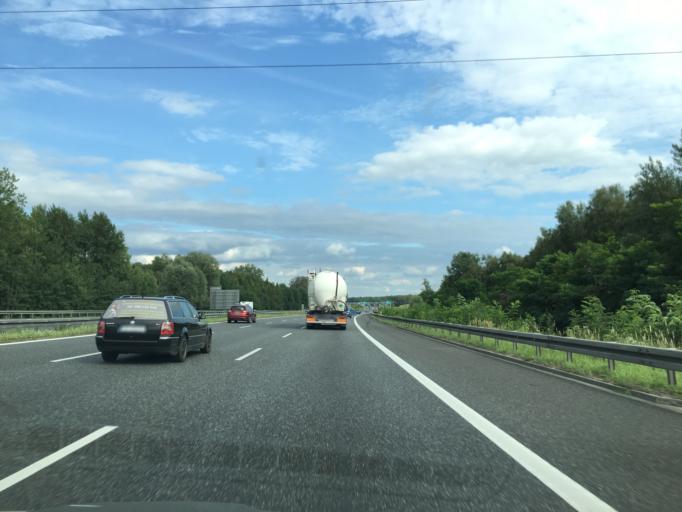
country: PL
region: Silesian Voivodeship
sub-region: Powiat gliwicki
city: Przyszowice
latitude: 50.2677
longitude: 18.7732
